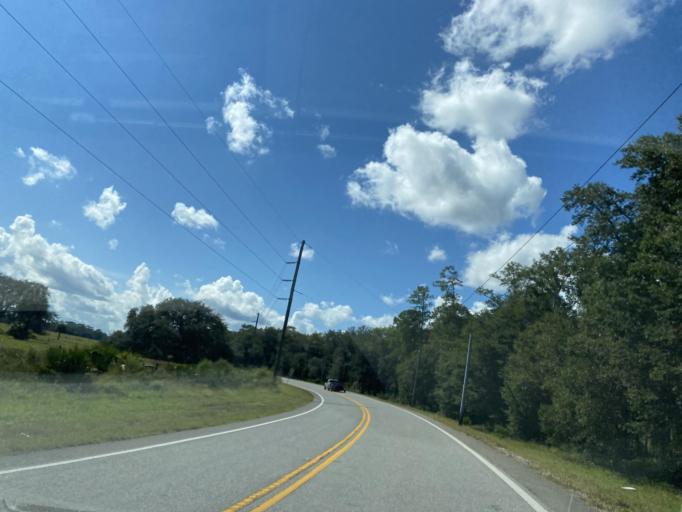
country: US
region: Florida
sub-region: Lake County
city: Umatilla
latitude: 28.9749
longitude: -81.5529
